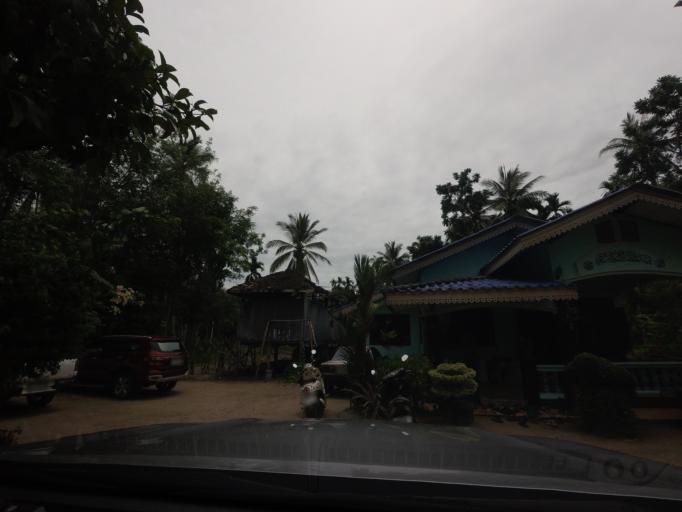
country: TH
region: Pattani
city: Sai Buri
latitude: 6.7046
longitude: 101.5353
